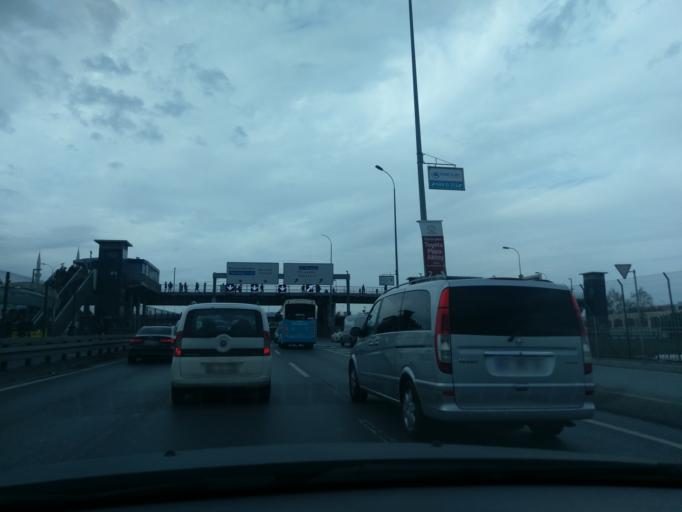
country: TR
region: Istanbul
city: Yakuplu
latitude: 40.9836
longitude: 28.7262
